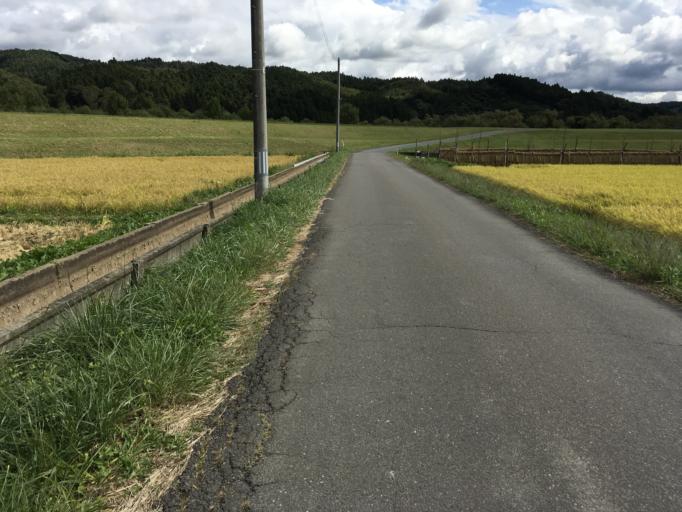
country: JP
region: Miyagi
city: Wakuya
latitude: 38.7279
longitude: 141.2914
